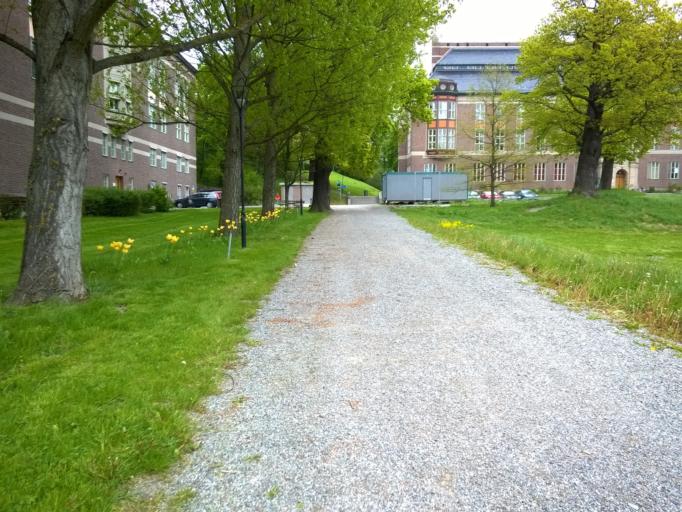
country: SE
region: Stockholm
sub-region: Norrtalje Kommun
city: Bergshamra
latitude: 59.3681
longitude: 18.0543
